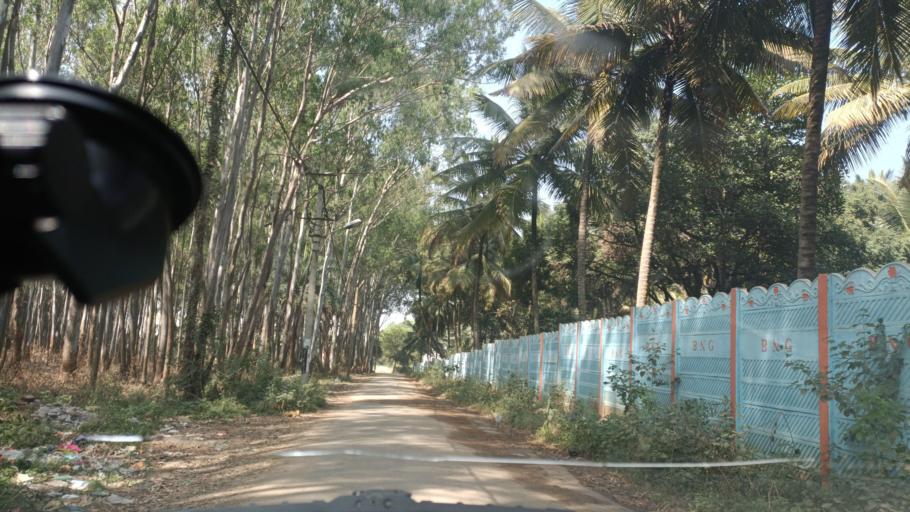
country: IN
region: Karnataka
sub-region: Bangalore Urban
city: Yelahanka
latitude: 13.1167
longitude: 77.6028
